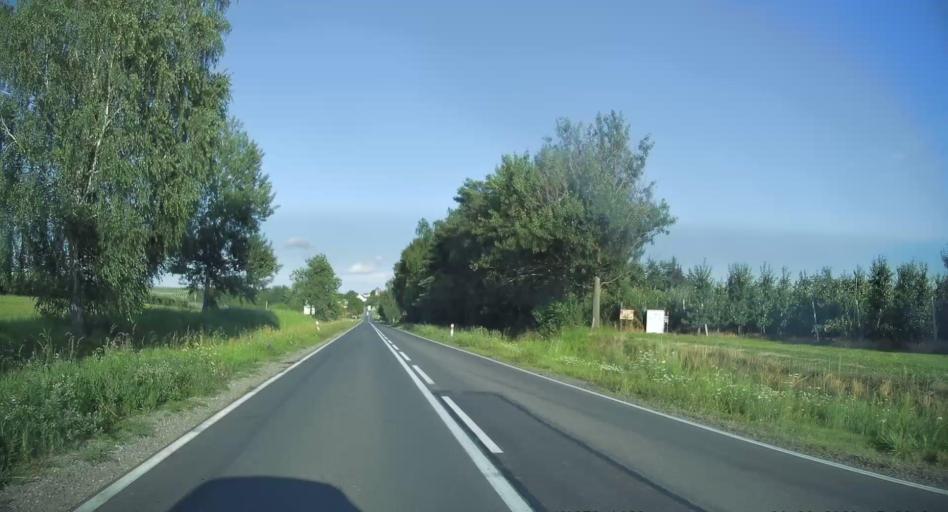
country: PL
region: Masovian Voivodeship
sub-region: Powiat grojecki
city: Bledow
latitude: 51.8018
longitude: 20.6110
